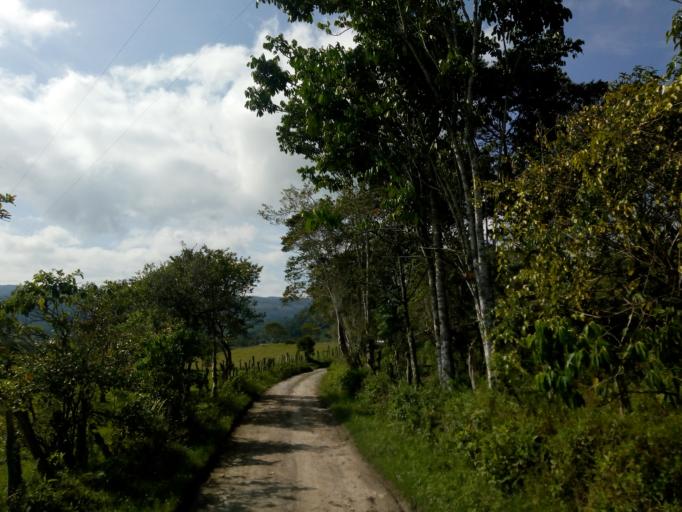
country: CO
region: Boyaca
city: Moniquira
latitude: 5.8800
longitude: -73.5077
